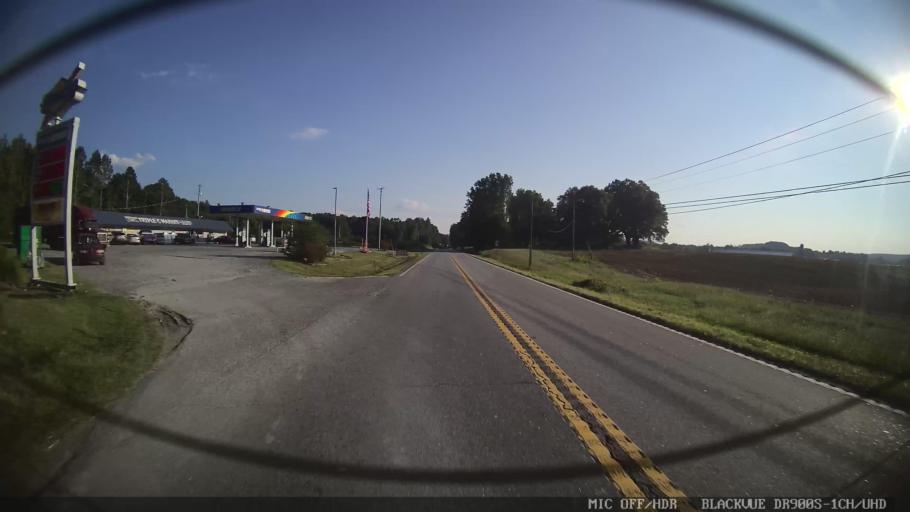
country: US
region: Tennessee
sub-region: Bradley County
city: Wildwood Lake
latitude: 34.9596
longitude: -84.7736
